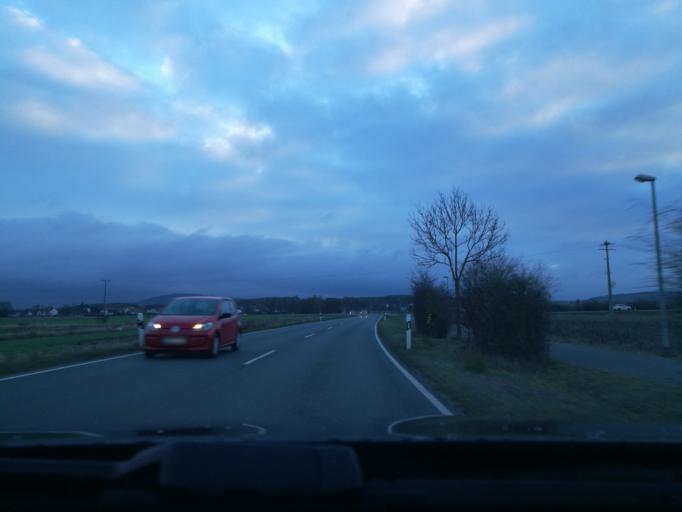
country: DE
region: Bavaria
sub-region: Regierungsbezirk Mittelfranken
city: Baiersdorf
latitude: 49.6567
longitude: 11.0455
